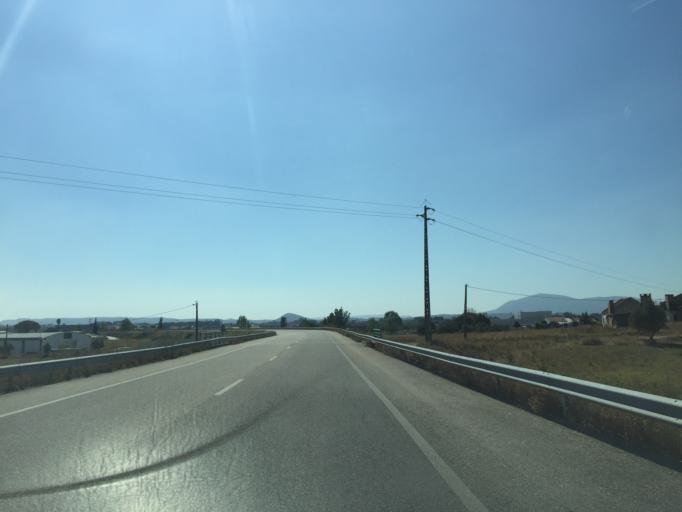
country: PT
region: Lisbon
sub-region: Azambuja
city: Aveiras de Cima
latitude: 39.1494
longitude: -8.8954
